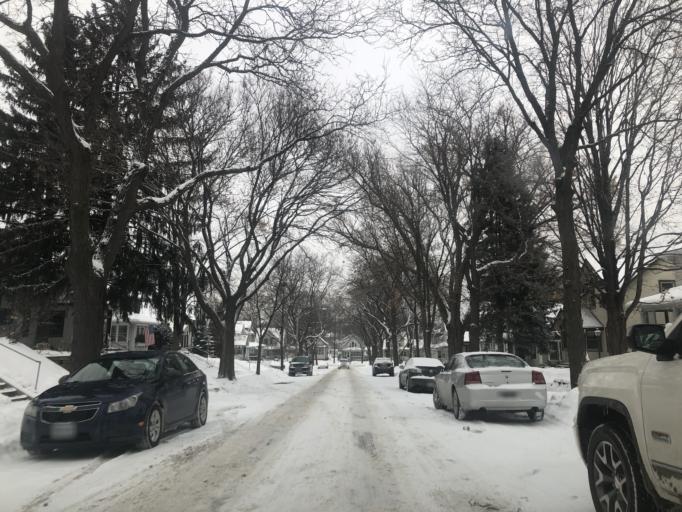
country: US
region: Minnesota
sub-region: Hennepin County
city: Richfield
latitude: 44.9292
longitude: -93.2805
